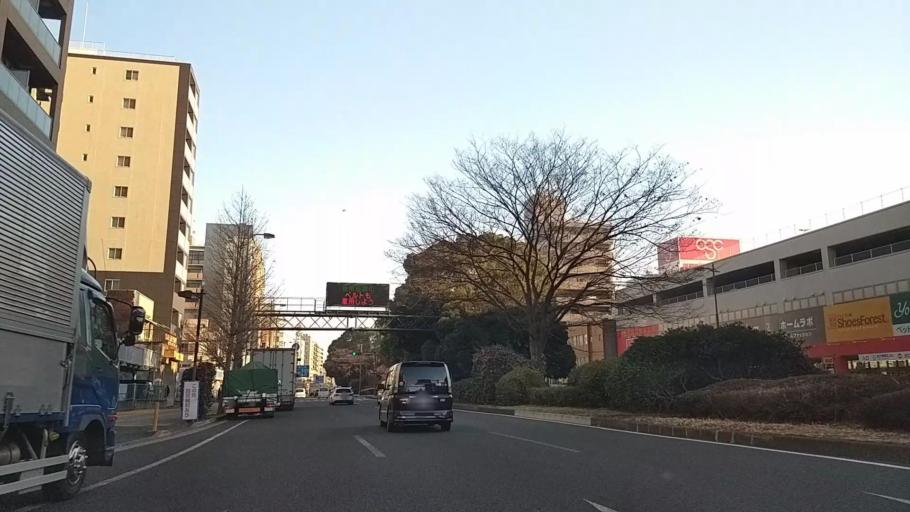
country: JP
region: Kanagawa
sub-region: Kawasaki-shi
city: Kawasaki
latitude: 35.5054
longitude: 139.6790
